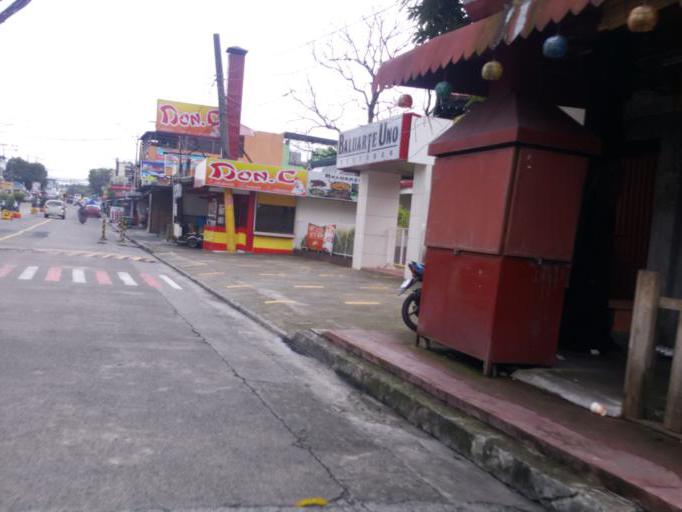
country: PH
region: Calabarzon
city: Bagong Pagasa
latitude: 14.7034
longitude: 121.0224
